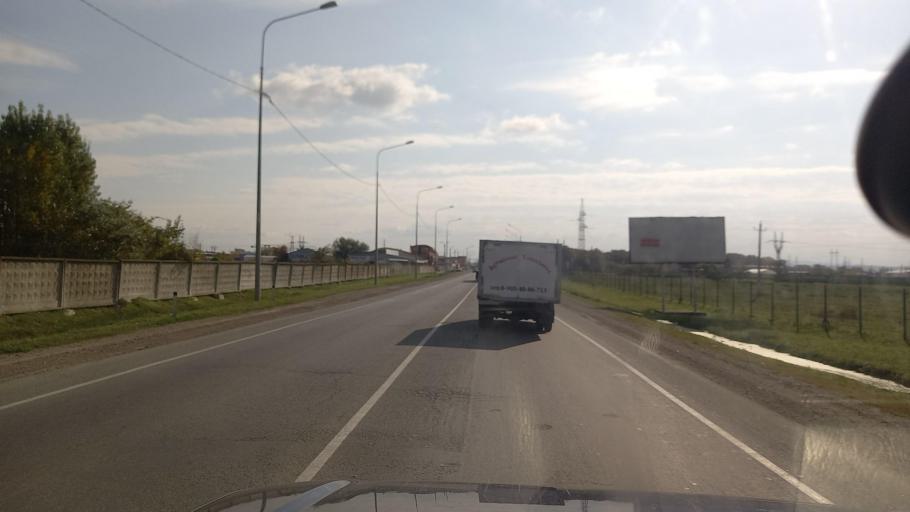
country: RU
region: Krasnodarskiy
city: Krymsk
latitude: 44.9112
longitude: 38.0178
